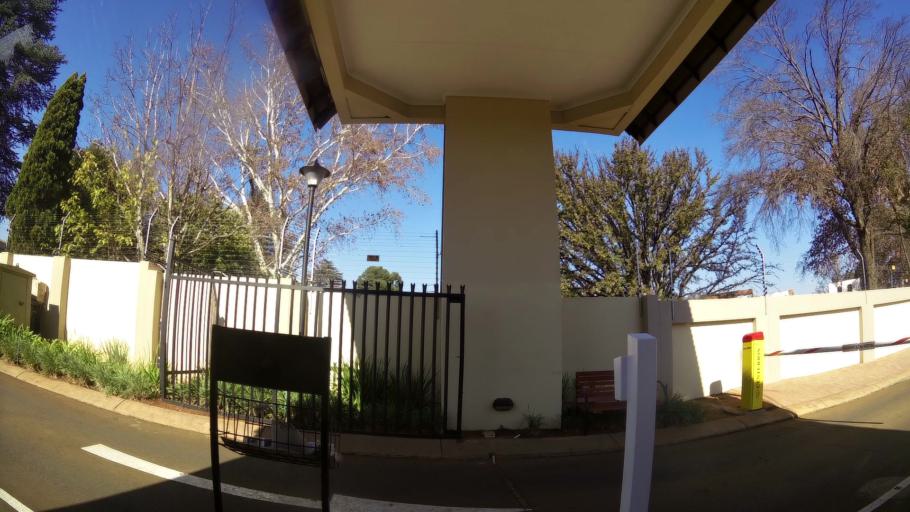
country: ZA
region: Gauteng
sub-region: City of Tshwane Metropolitan Municipality
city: Centurion
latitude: -25.8295
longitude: 28.1688
